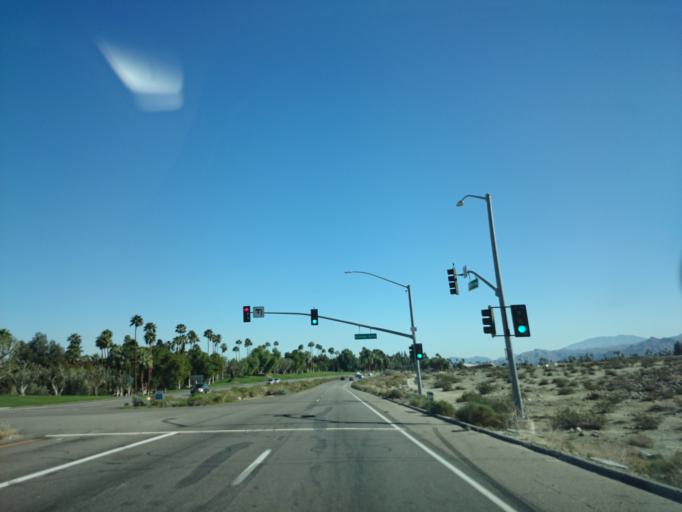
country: US
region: California
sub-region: Riverside County
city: Palm Springs
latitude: 33.8614
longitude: -116.5617
